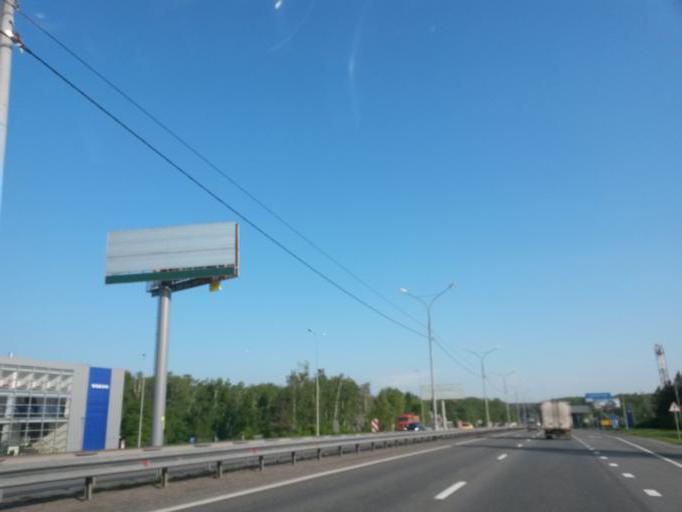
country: RU
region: Moskovskaya
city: Petrovskaya
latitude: 55.5310
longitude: 37.8139
